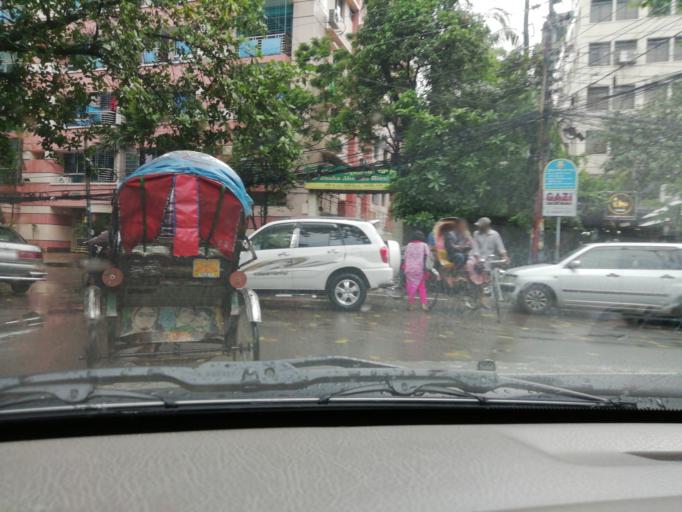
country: BD
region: Dhaka
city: Azimpur
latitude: 23.7522
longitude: 90.3757
